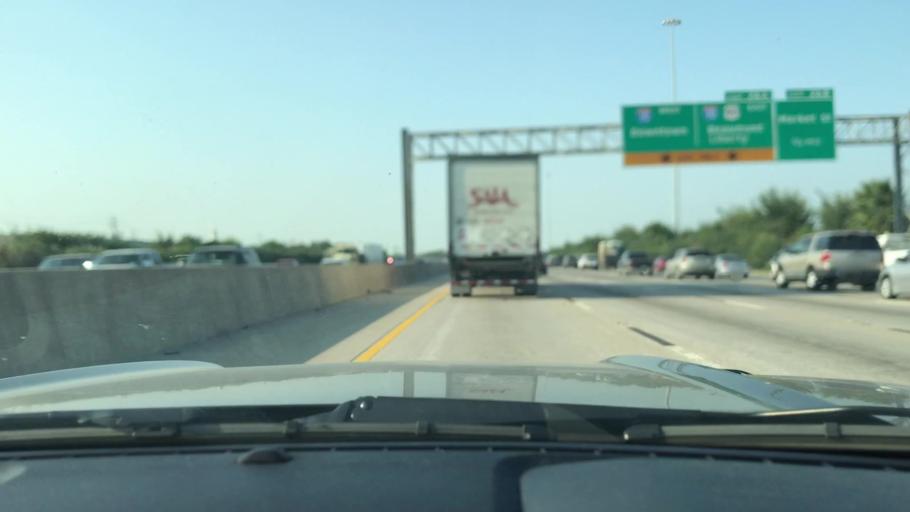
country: US
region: Texas
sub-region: Harris County
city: Jacinto City
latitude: 29.7558
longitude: -95.2651
